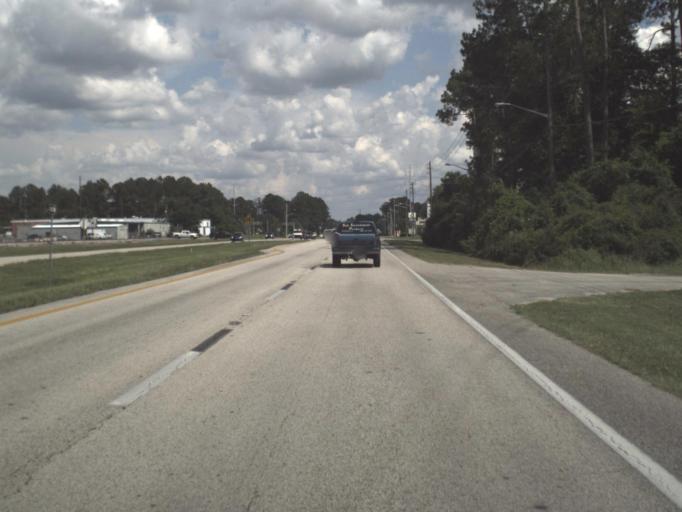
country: US
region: Florida
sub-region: Alachua County
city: Gainesville
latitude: 29.7061
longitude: -82.3472
